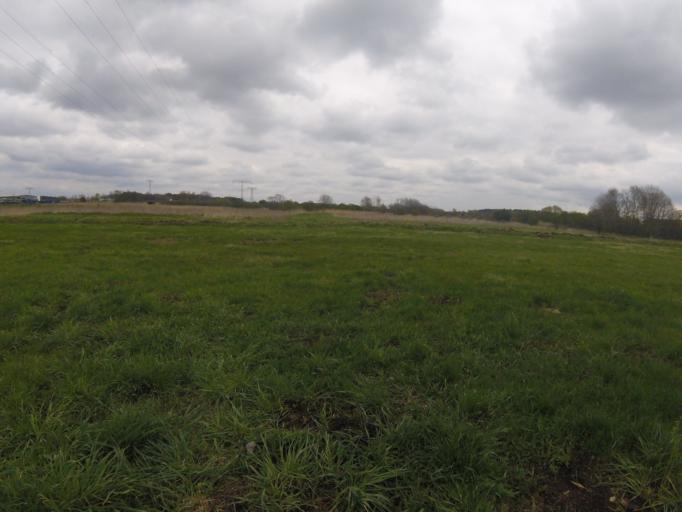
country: DE
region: Brandenburg
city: Mittenwalde
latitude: 52.2581
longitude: 13.5742
